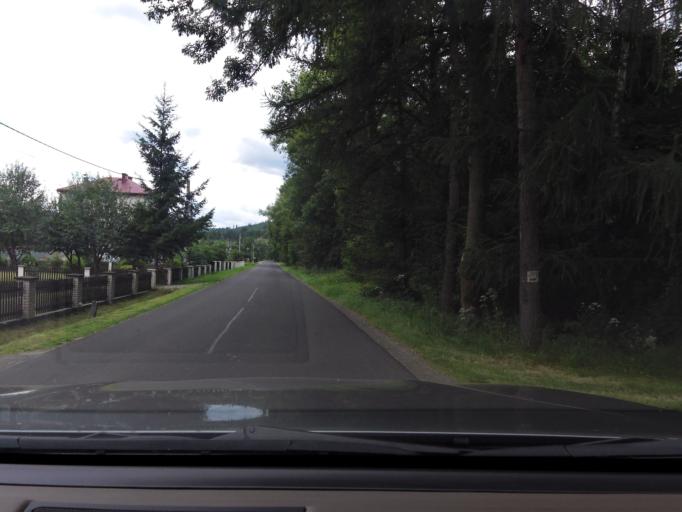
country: PL
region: Silesian Voivodeship
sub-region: Powiat zywiecki
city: Ujsoly
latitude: 49.4901
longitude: 19.1221
